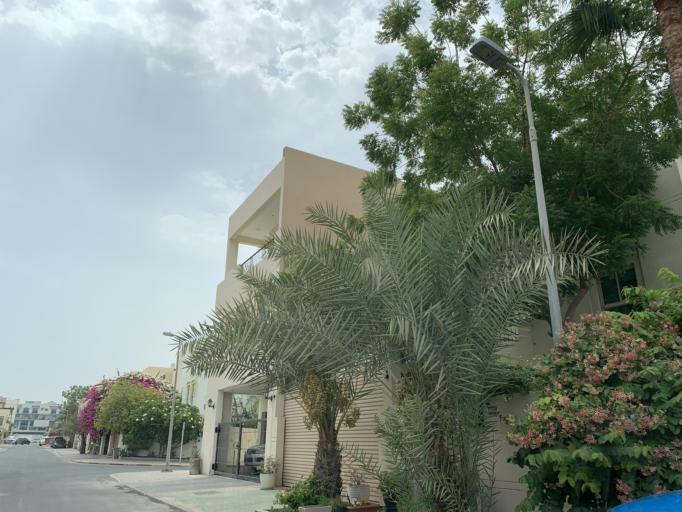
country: BH
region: Northern
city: Madinat `Isa
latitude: 26.1815
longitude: 50.4779
